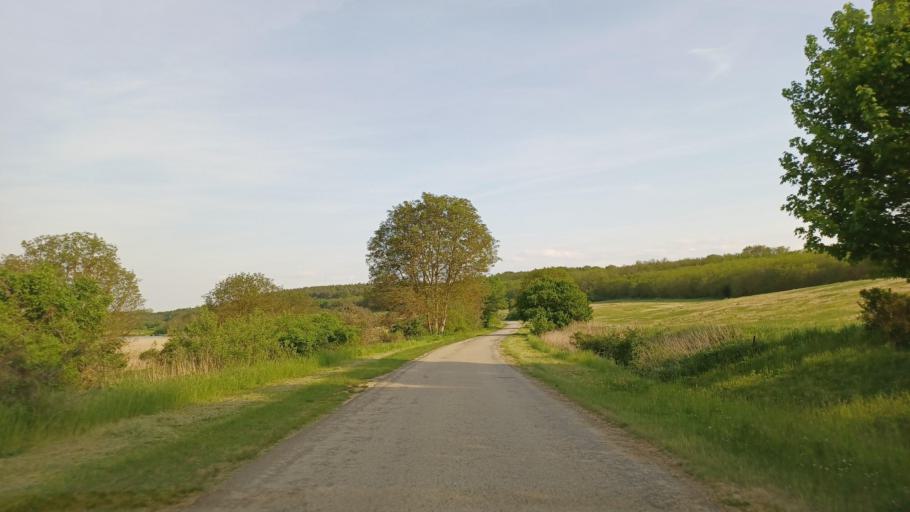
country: HU
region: Baranya
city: Kozarmisleny
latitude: 45.9673
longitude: 18.3660
